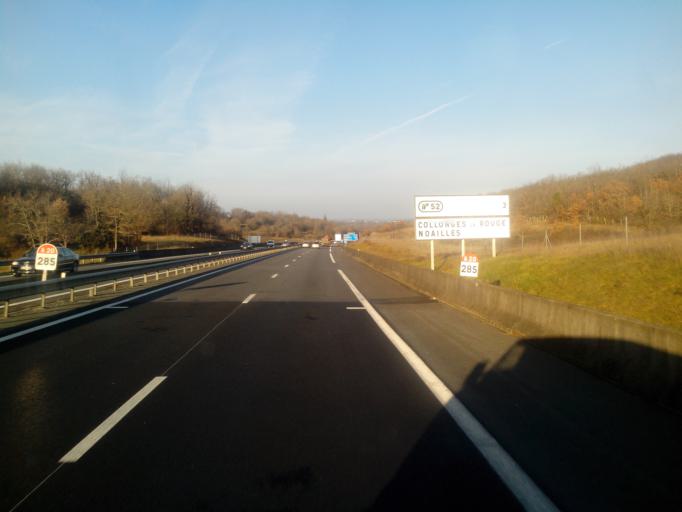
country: FR
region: Limousin
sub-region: Departement de la Correze
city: Brive-la-Gaillarde
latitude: 45.0683
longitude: 1.5081
